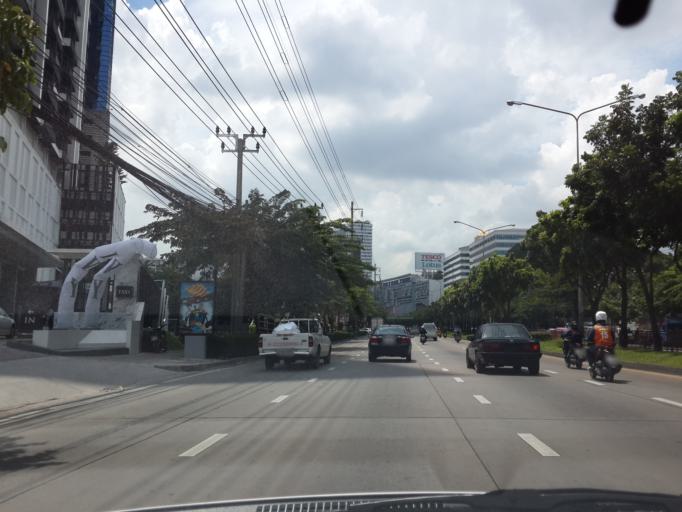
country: TH
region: Bangkok
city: Din Daeng
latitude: 13.7634
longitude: 100.5681
